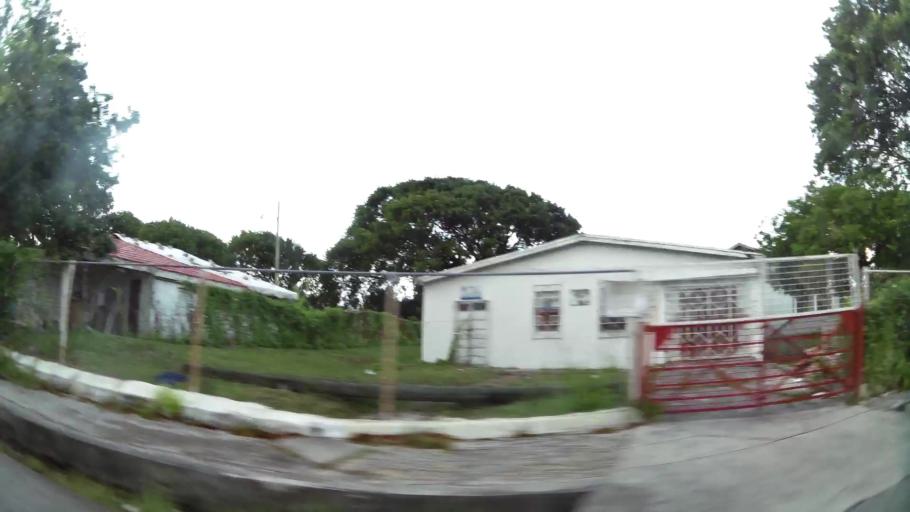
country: AG
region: Saint John
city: Saint John's
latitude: 17.1235
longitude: -61.8389
